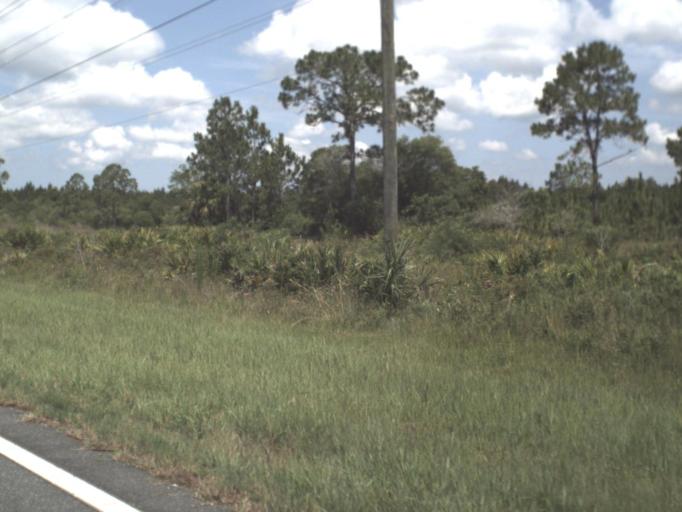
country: US
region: Florida
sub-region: Levy County
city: Chiefland
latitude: 29.2450
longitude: -82.9185
